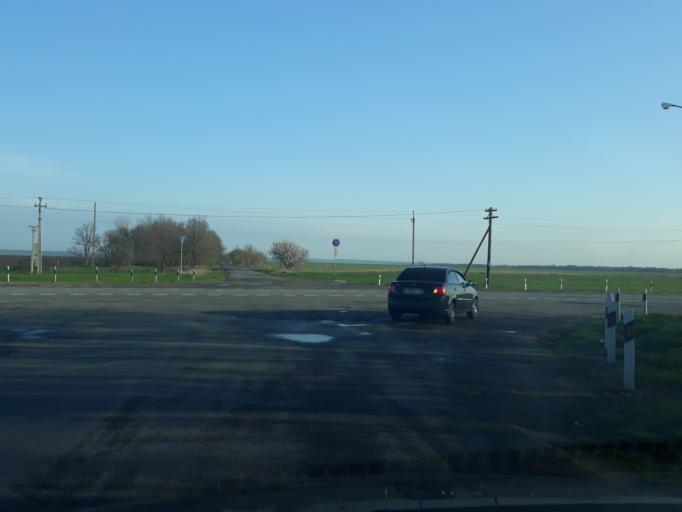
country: RU
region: Rostov
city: Novobessergenovka
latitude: 47.1880
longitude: 38.6201
